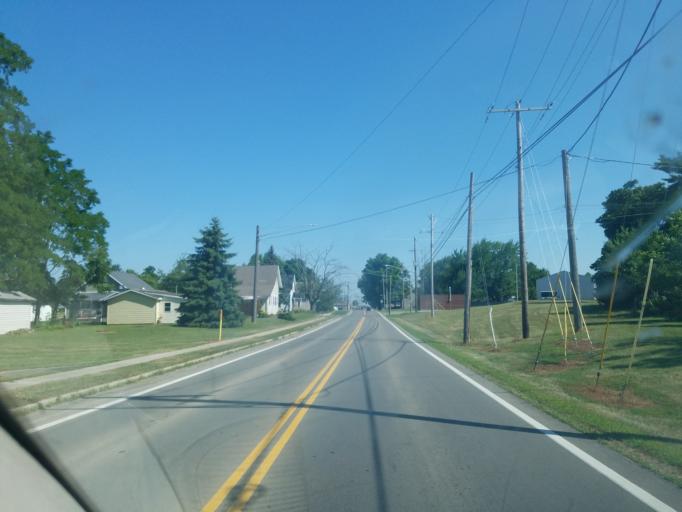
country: US
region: Ohio
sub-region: Logan County
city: Northwood
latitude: 40.4411
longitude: -83.8056
